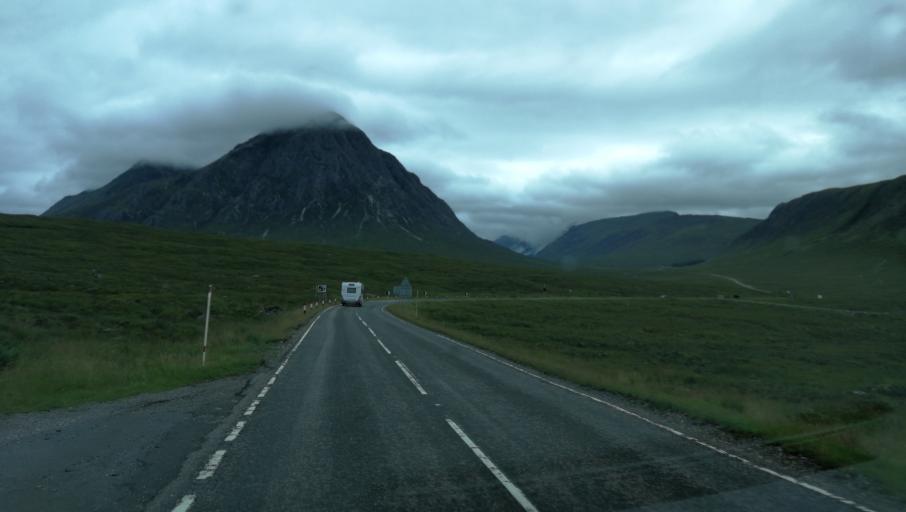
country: GB
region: Scotland
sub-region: Highland
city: Spean Bridge
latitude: 56.6469
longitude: -4.8392
